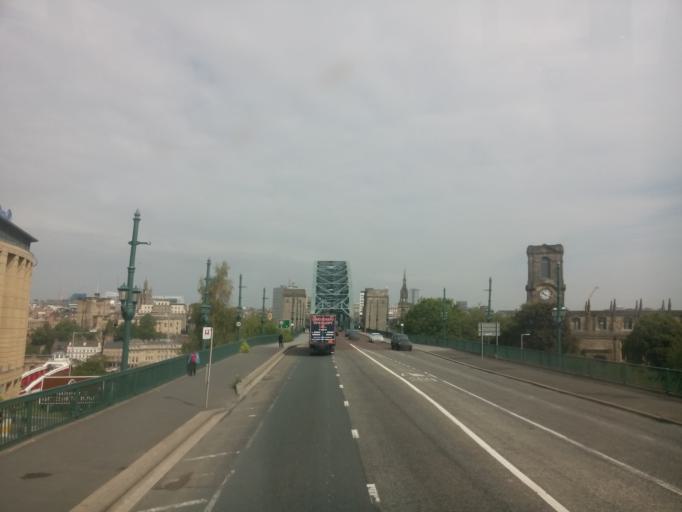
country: GB
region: England
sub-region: Gateshead
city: Gateshead
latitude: 54.9660
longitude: -1.6040
